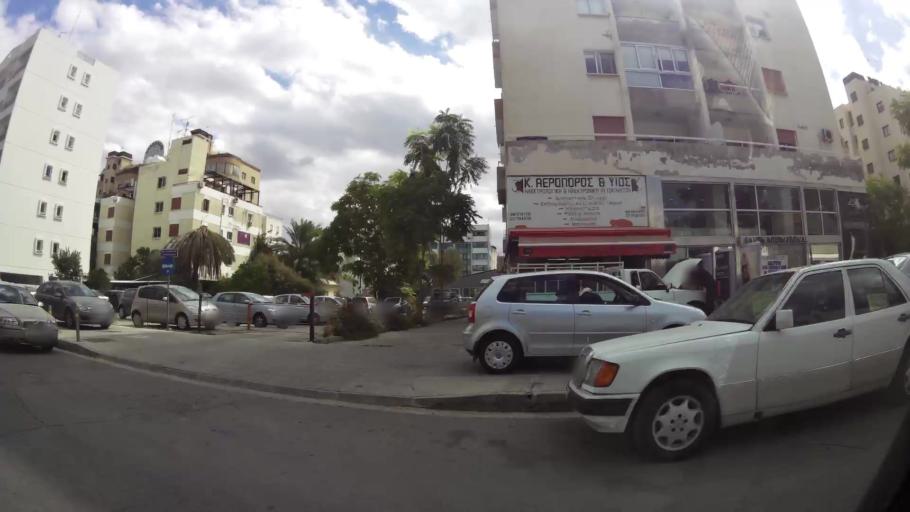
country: CY
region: Lefkosia
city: Nicosia
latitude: 35.1614
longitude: 33.3602
